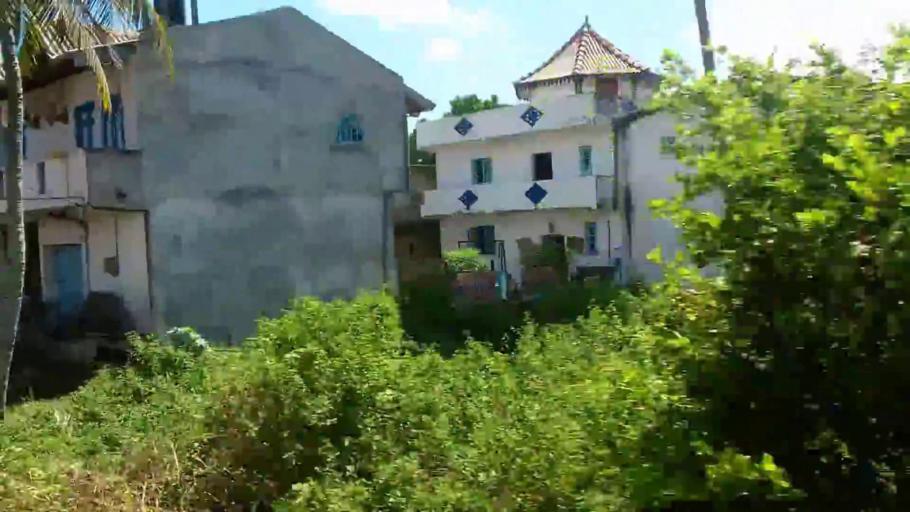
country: LK
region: Southern
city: Hikkaduwa
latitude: 6.1606
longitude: 80.0937
